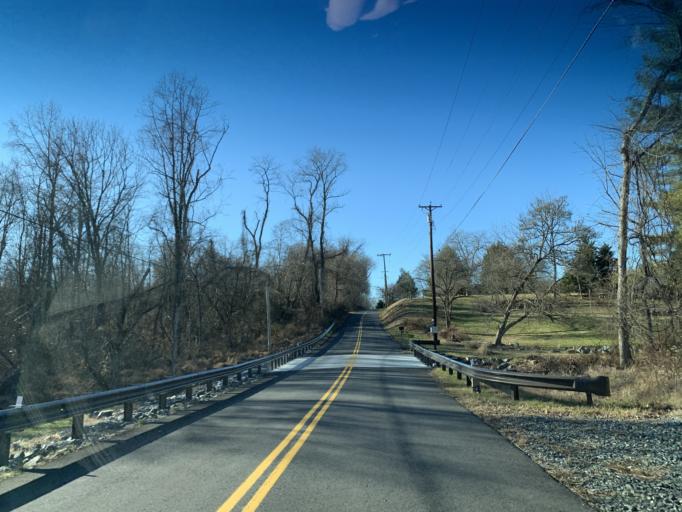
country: US
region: Maryland
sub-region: Harford County
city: Riverside
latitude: 39.5350
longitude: -76.2560
